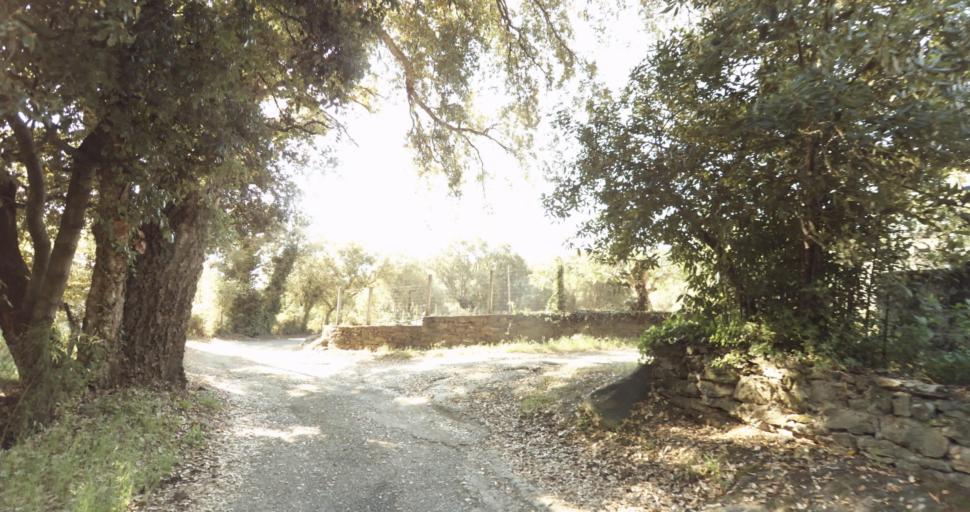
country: FR
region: Corsica
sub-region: Departement de la Haute-Corse
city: Biguglia
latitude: 42.6293
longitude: 9.4244
